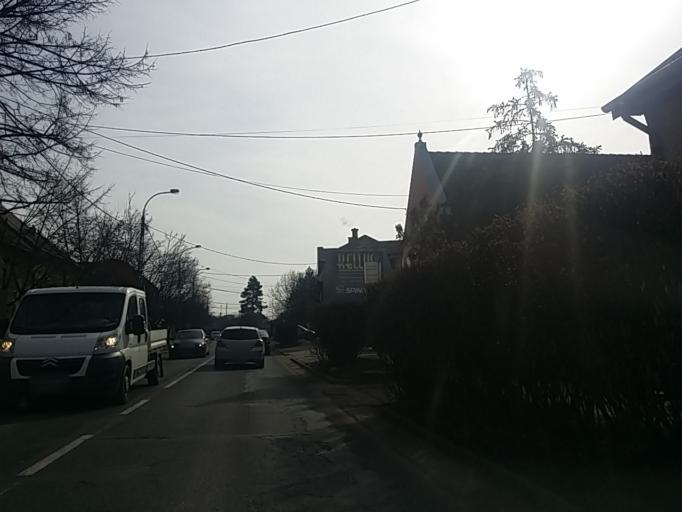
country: HU
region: Pest
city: Dunakeszi
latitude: 47.6298
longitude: 19.1311
